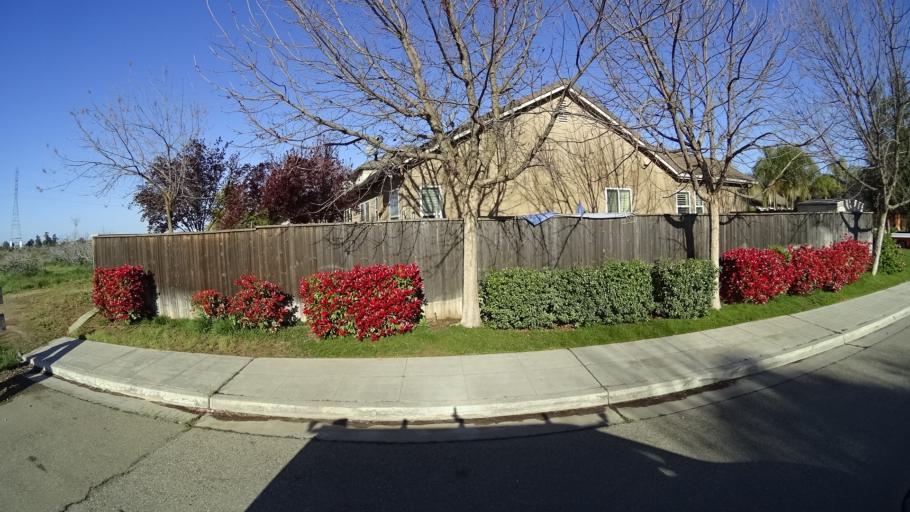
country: US
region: California
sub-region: Fresno County
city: Biola
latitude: 36.8299
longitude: -119.9008
